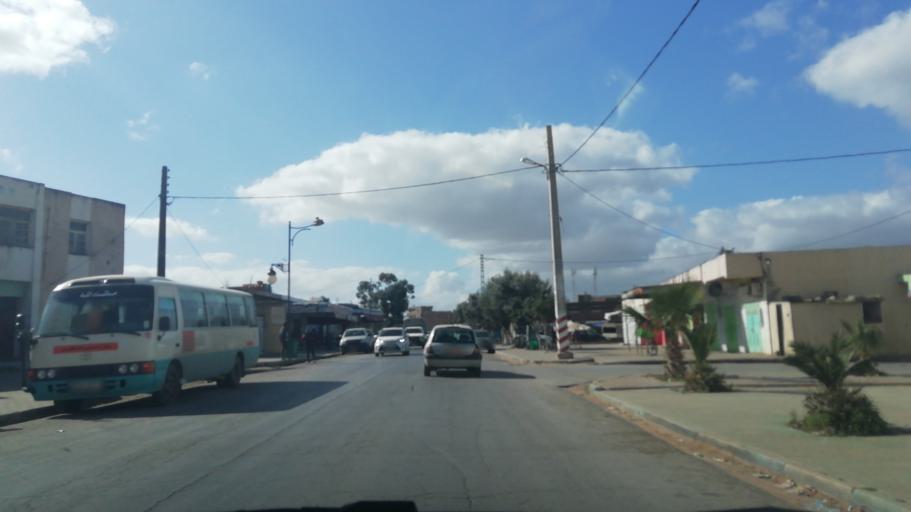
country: DZ
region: Relizane
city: Mazouna
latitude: 36.2720
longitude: 0.6331
